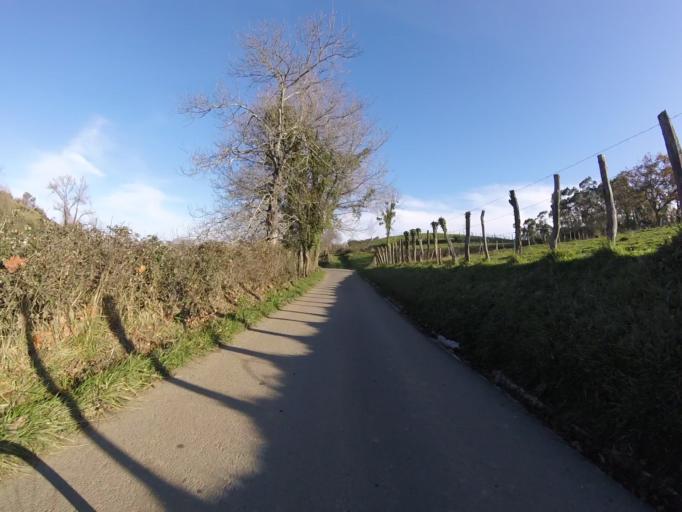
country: ES
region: Basque Country
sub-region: Provincia de Guipuzcoa
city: Astigarraga
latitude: 43.2710
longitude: -1.9277
